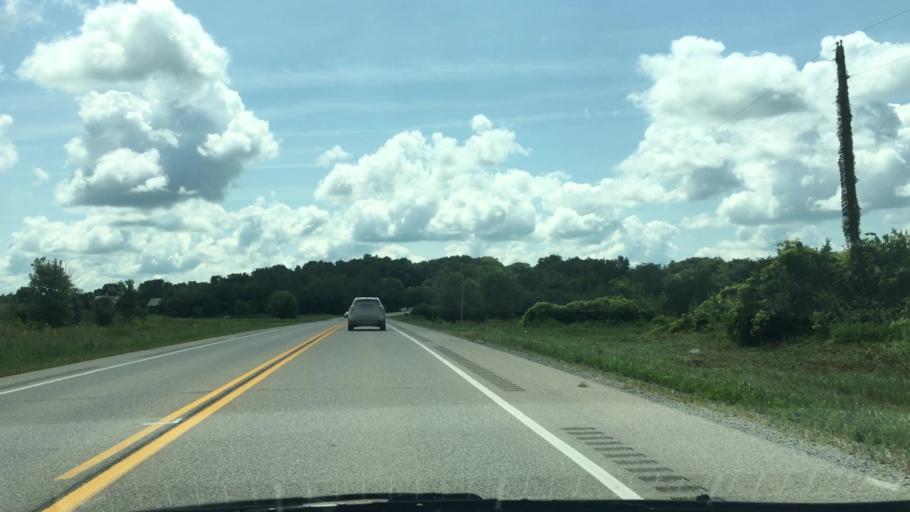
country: US
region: Iowa
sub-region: Johnson County
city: Solon
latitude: 41.7532
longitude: -91.4752
